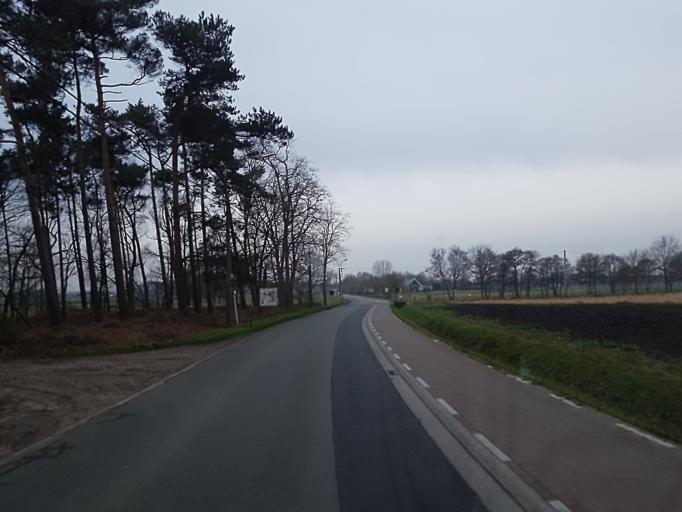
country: BE
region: Flanders
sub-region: Provincie Oost-Vlaanderen
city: Waarschoot
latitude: 51.1734
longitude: 3.6197
